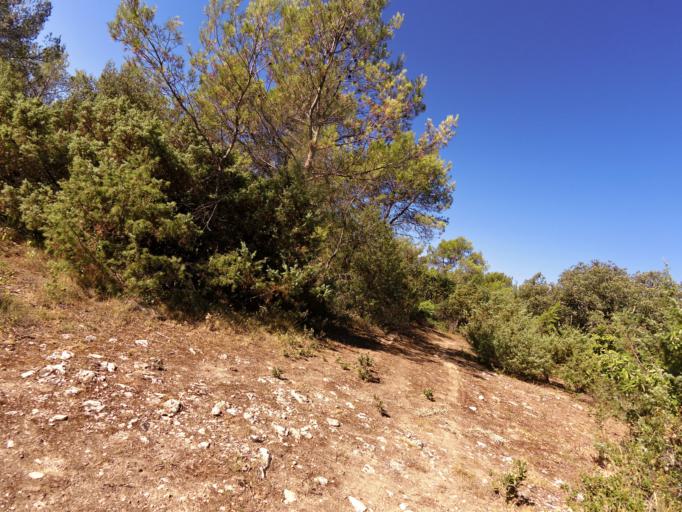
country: FR
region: Languedoc-Roussillon
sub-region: Departement du Gard
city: Congenies
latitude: 43.7617
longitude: 4.1865
